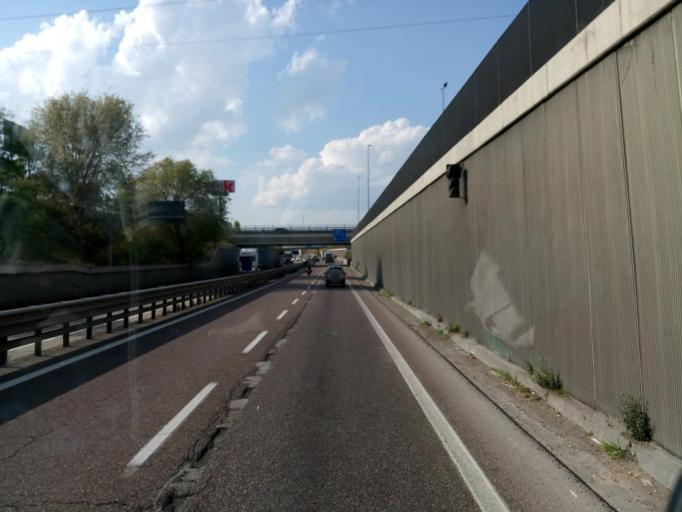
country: IT
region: Veneto
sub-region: Provincia di Verona
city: San Giovanni Lupatoto
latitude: 45.3960
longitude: 11.0164
